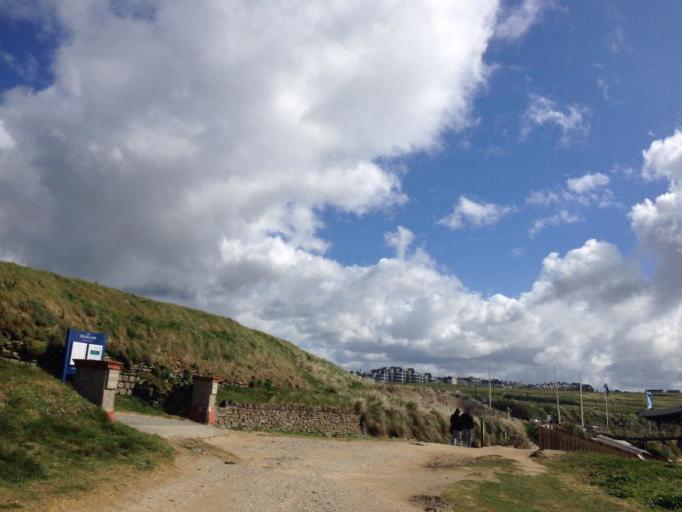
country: GB
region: England
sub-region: Cornwall
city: Newquay
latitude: 50.4195
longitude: -5.0973
